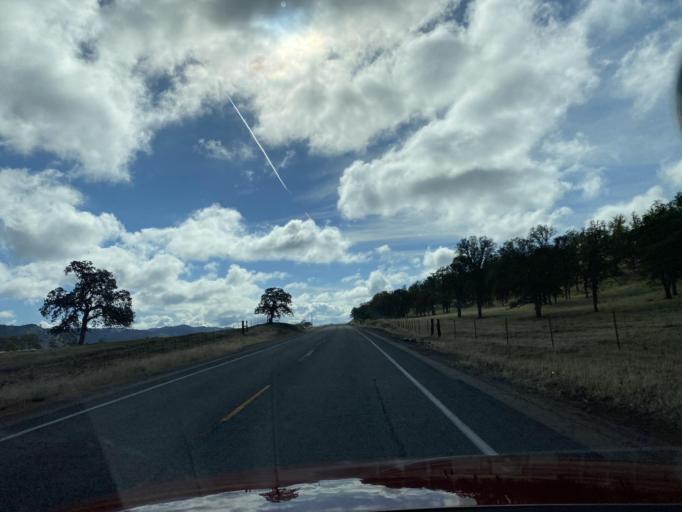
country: US
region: California
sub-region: Glenn County
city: Willows
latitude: 39.5367
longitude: -122.5347
